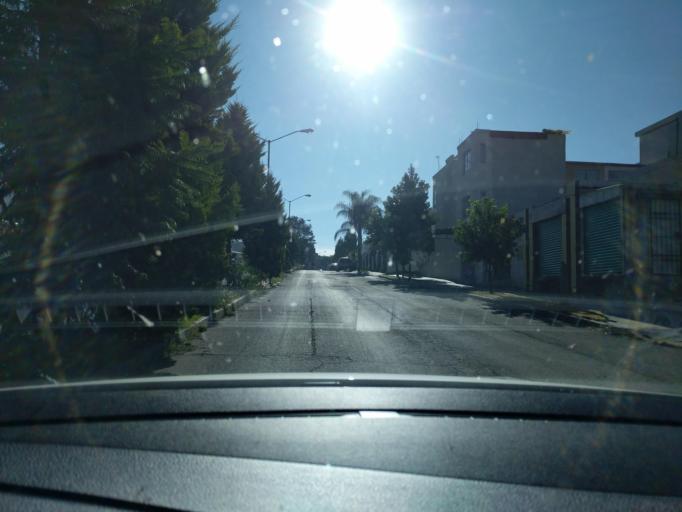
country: MX
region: Puebla
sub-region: Huejotzingo
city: Los Encinos
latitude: 19.1772
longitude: -98.3923
